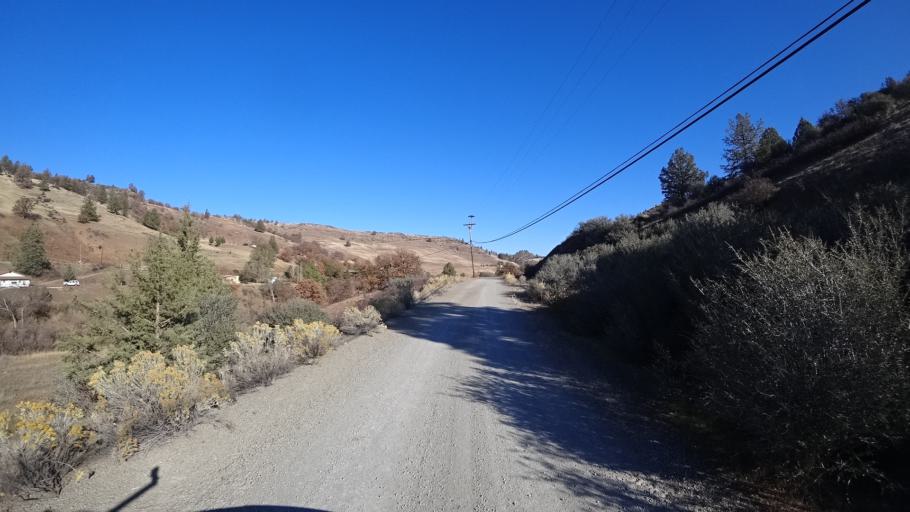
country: US
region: California
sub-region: Siskiyou County
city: Montague
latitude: 41.9201
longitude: -122.4486
